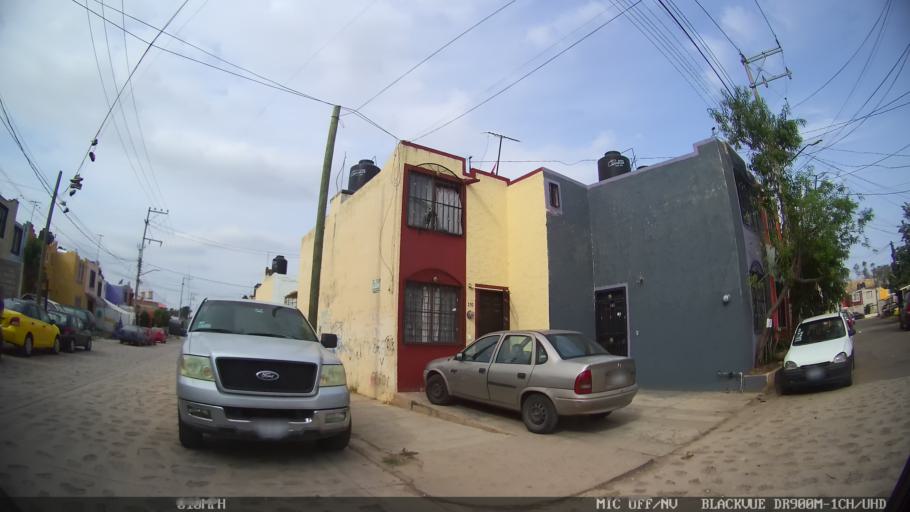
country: MX
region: Jalisco
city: Tonala
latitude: 20.6338
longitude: -103.2343
